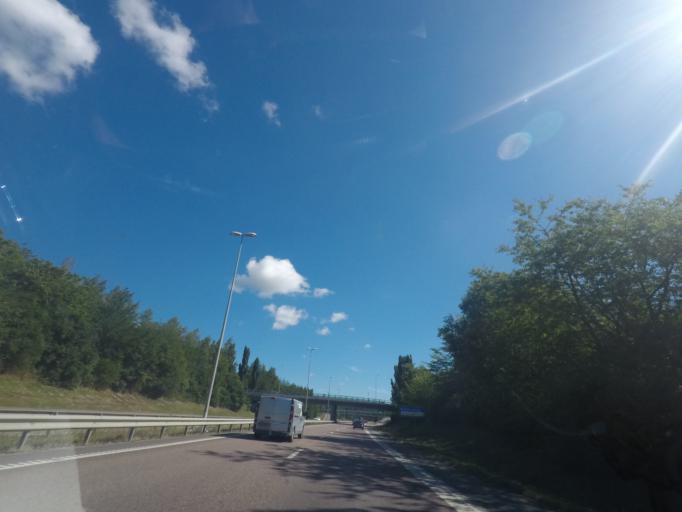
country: SE
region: Uppsala
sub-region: Uppsala Kommun
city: Gamla Uppsala
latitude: 59.8788
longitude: 17.6150
